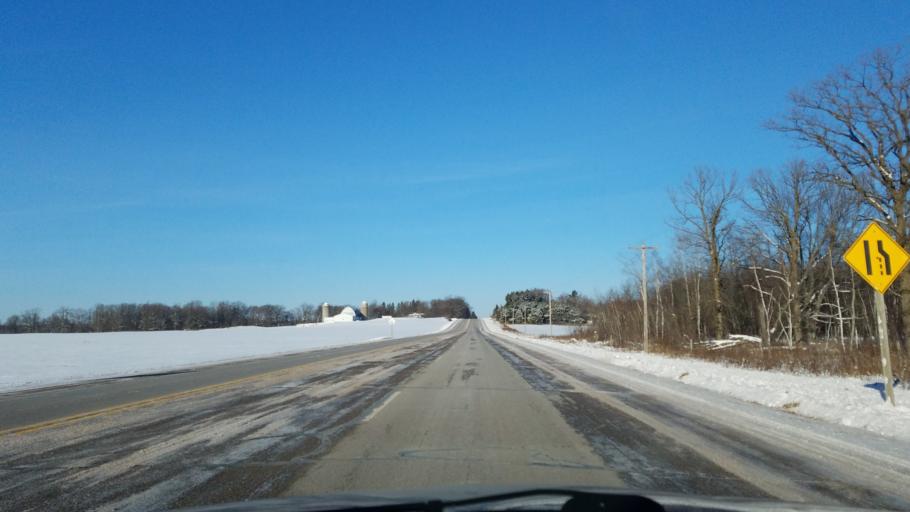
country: US
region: Wisconsin
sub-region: Barron County
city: Cumberland
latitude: 45.4981
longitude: -92.0525
